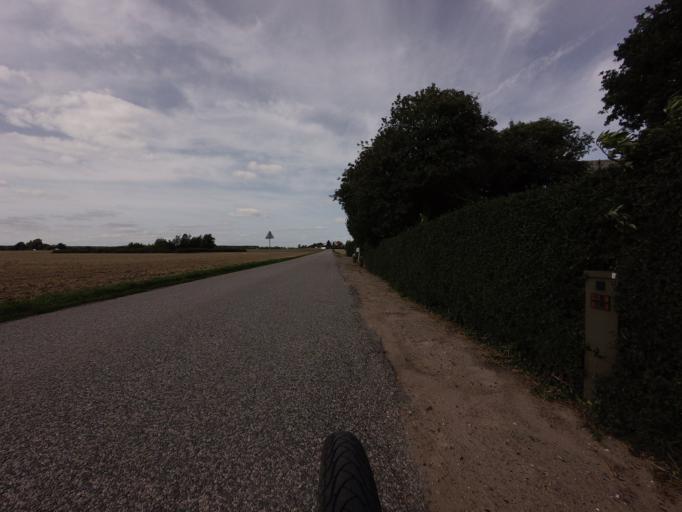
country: DK
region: Zealand
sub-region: Faxe Kommune
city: Fakse Ladeplads
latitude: 55.2501
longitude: 12.2626
